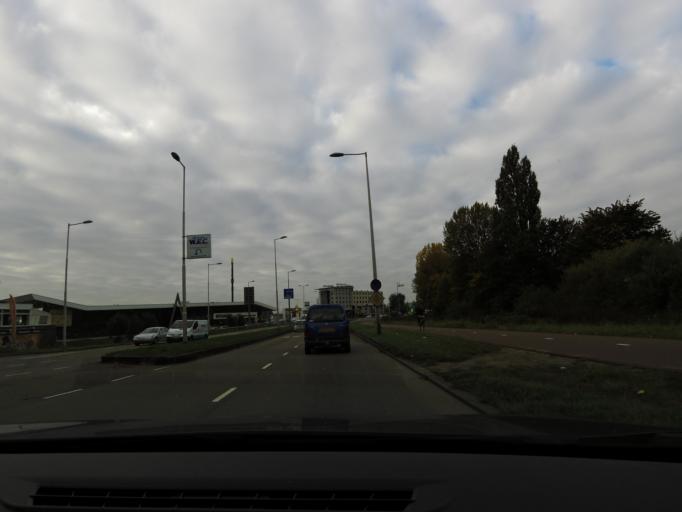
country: NL
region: South Holland
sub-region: Gemeente Rotterdam
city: Delfshaven
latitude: 51.8705
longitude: 4.4545
